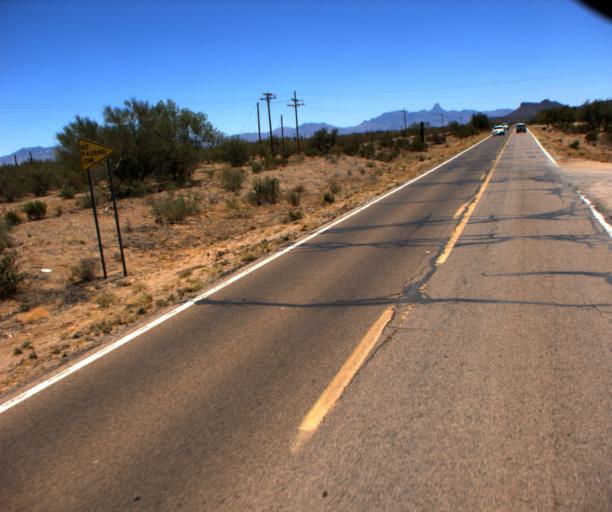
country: US
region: Arizona
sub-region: Pima County
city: Sells
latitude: 31.9357
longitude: -111.9148
